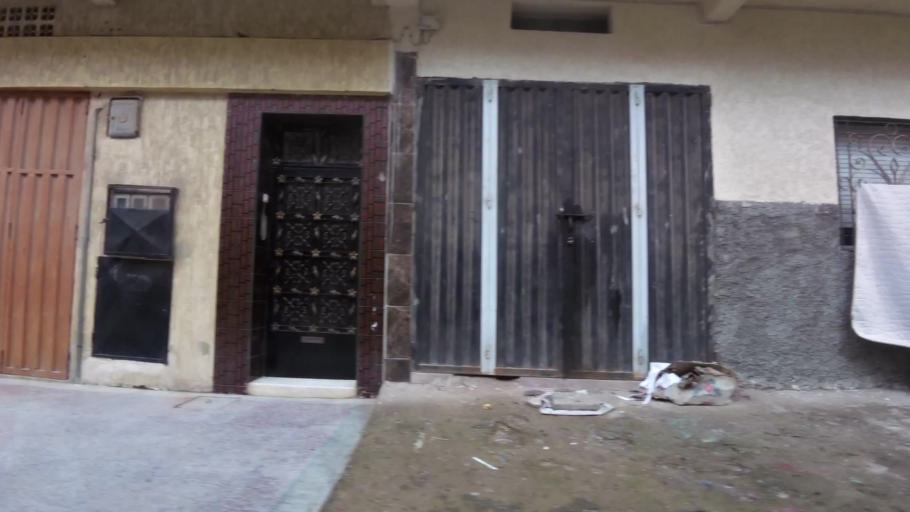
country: MA
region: Chaouia-Ouardigha
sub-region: Settat Province
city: Berrechid
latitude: 33.2723
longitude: -7.5896
